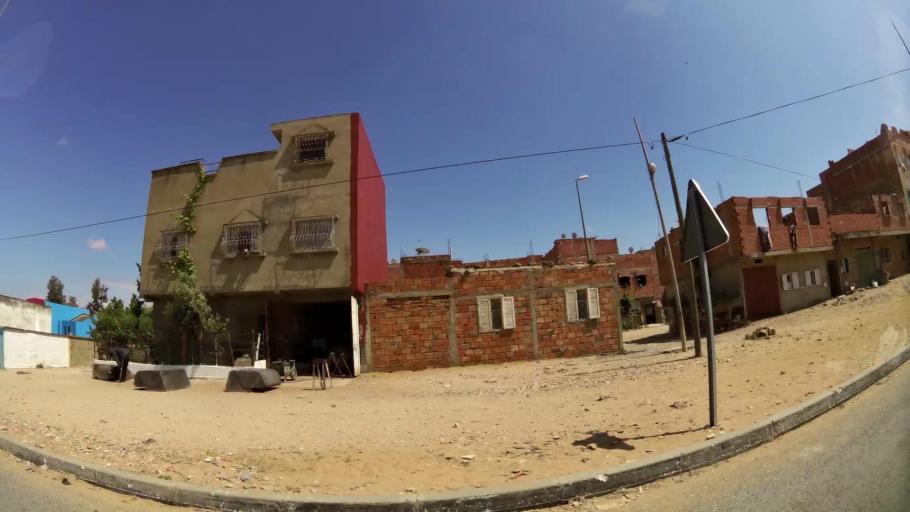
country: MA
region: Gharb-Chrarda-Beni Hssen
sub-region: Kenitra Province
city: Kenitra
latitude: 34.2307
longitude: -6.5420
